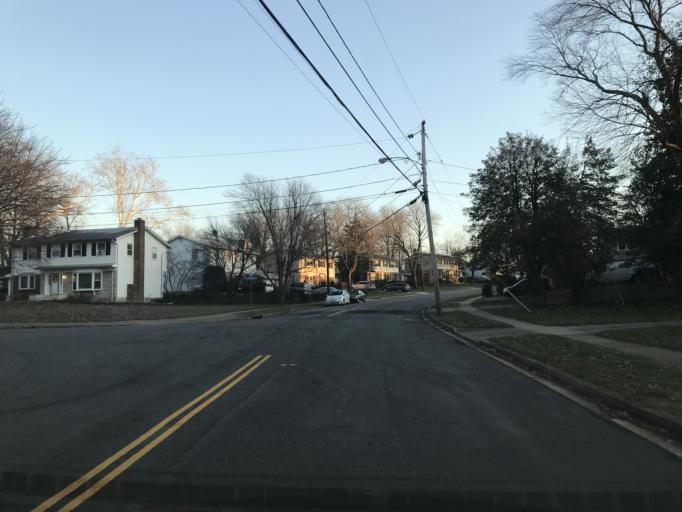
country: US
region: Virginia
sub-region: Fairfax County
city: Franconia
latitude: 38.7865
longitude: -77.1638
